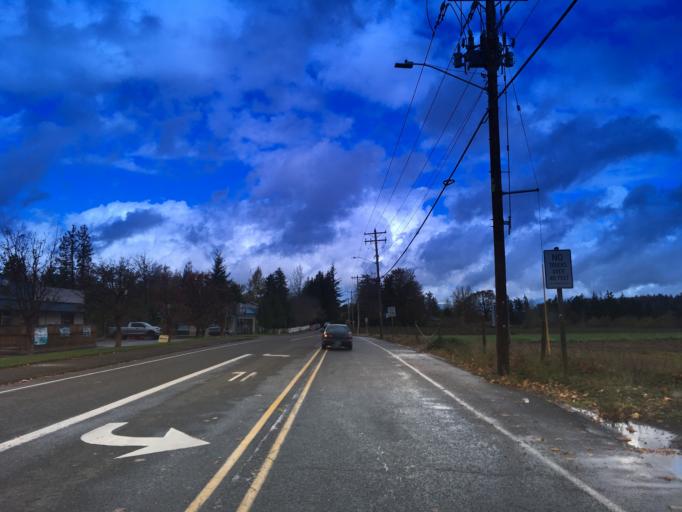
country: US
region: Oregon
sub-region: Multnomah County
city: Troutdale
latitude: 45.5191
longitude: -122.3869
